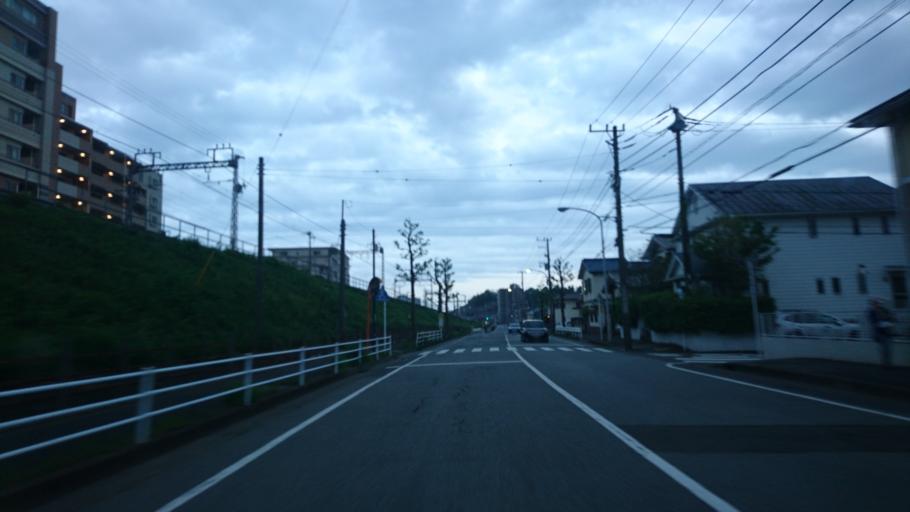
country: JP
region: Kanagawa
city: Fujisawa
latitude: 35.3559
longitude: 139.4736
